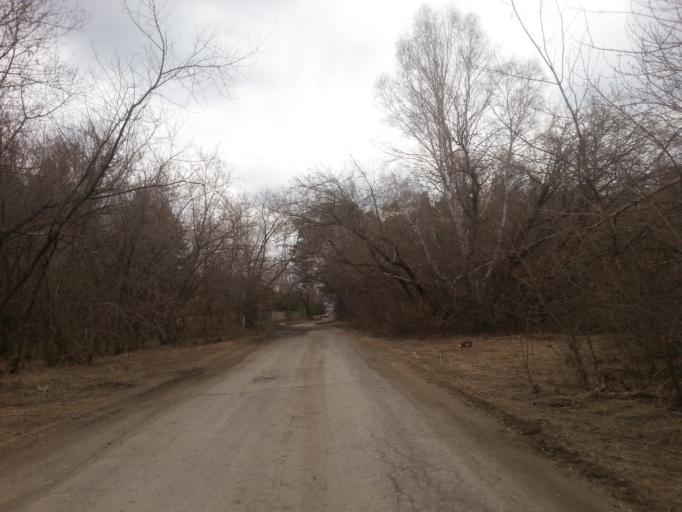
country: RU
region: Altai Krai
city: Yuzhnyy
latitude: 53.2868
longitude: 83.7299
